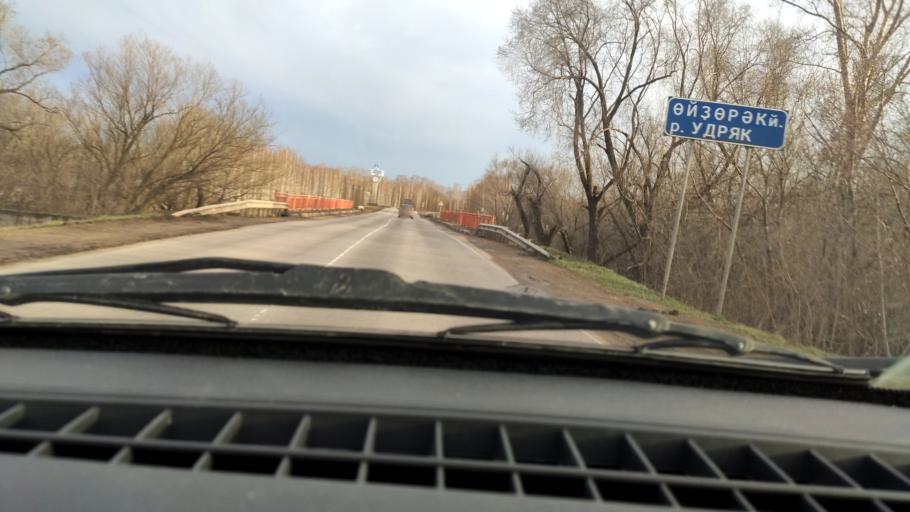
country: RU
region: Bashkortostan
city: Davlekanovo
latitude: 54.3662
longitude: 55.1953
